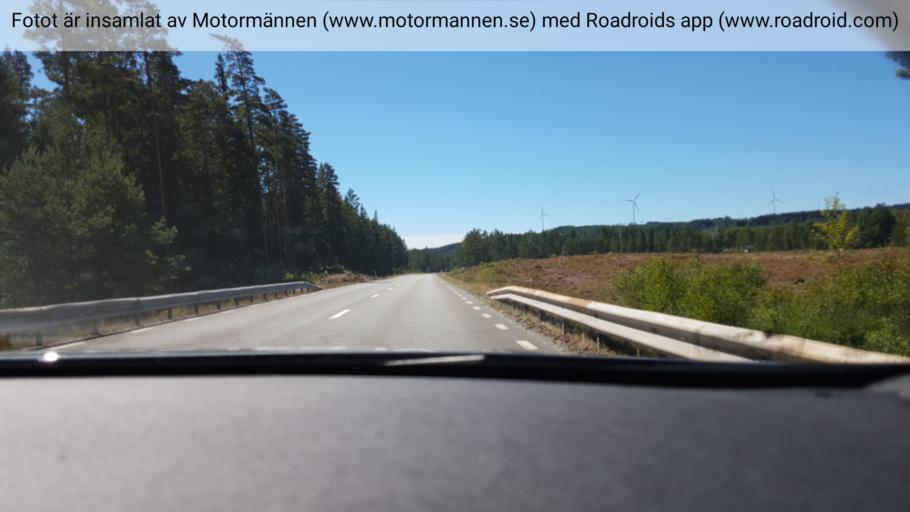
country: SE
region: Joenkoeping
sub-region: Mullsjo Kommun
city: Mullsjoe
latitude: 57.7699
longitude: 13.8329
